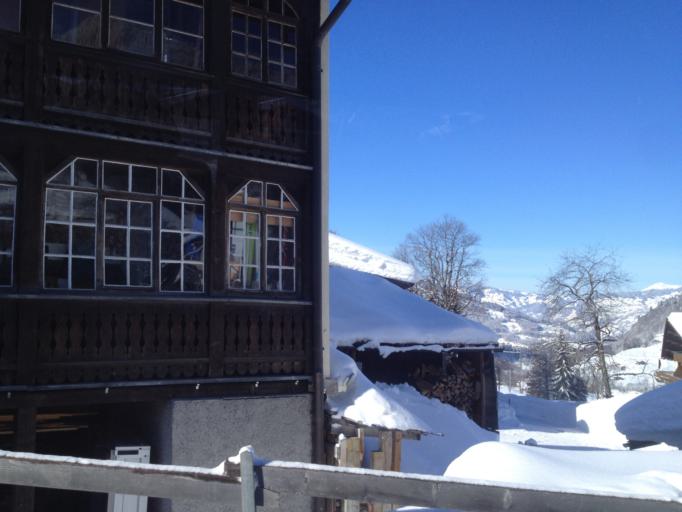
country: CH
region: Grisons
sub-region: Praettigau/Davos District
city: Klosters Serneus
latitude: 46.8775
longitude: 9.8792
